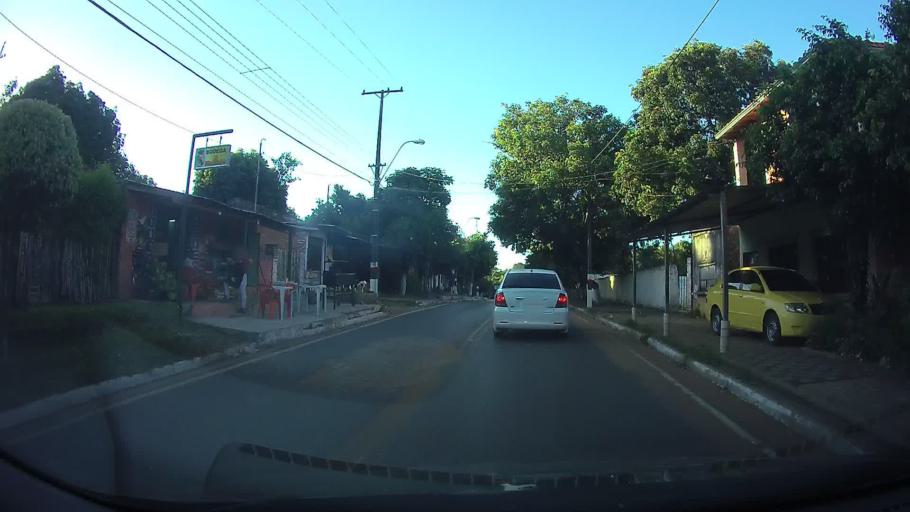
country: PY
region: Central
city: Aregua
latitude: -25.3146
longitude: -57.3913
